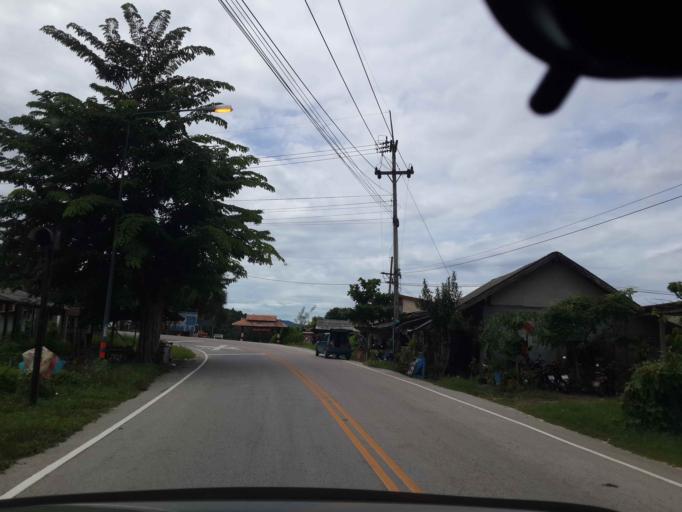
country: TH
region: Narathiwat
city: Rueso
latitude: 6.3595
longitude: 101.5380
